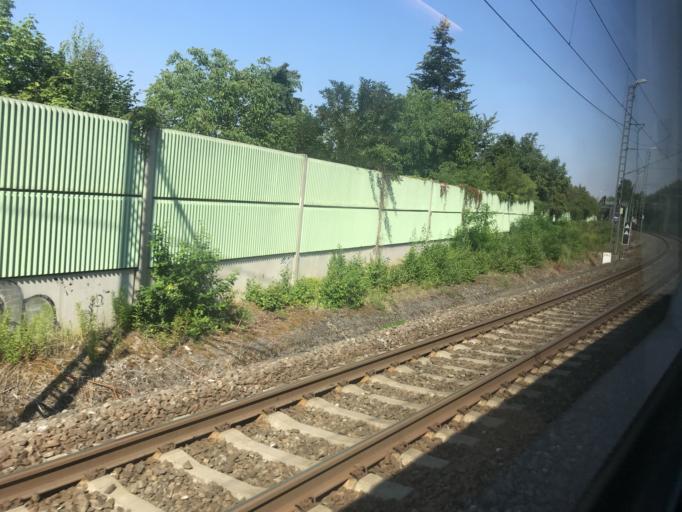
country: CZ
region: Central Bohemia
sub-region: Okres Praha-Vychod
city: Ricany
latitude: 49.9949
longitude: 14.6687
